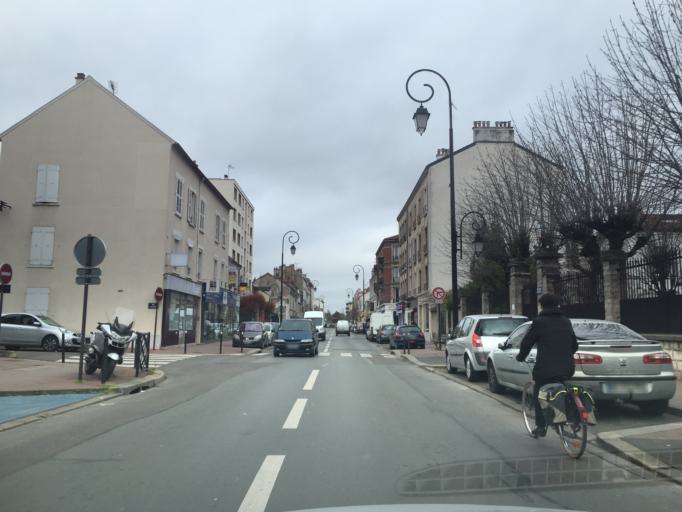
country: FR
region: Ile-de-France
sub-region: Departement du Val-de-Marne
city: Saint-Maur-des-Fosses
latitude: 48.7981
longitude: 2.4832
